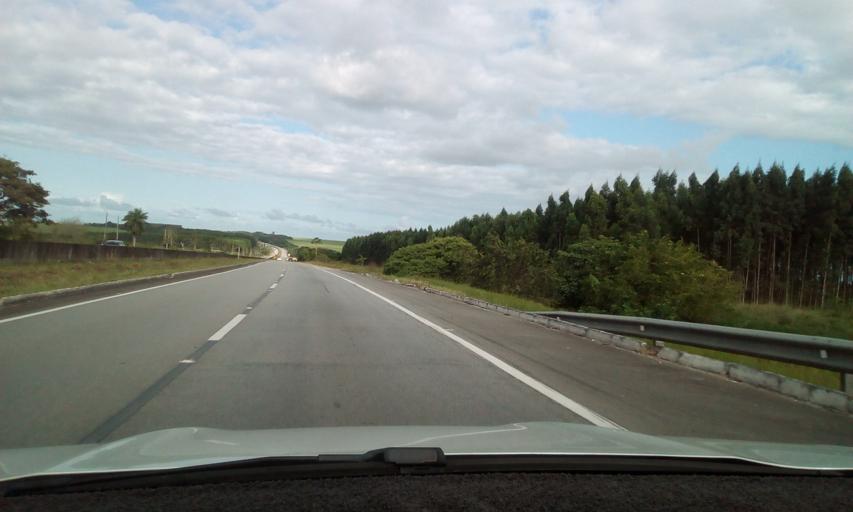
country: BR
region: Paraiba
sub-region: Santa Rita
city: Santa Rita
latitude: -7.0443
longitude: -35.0490
